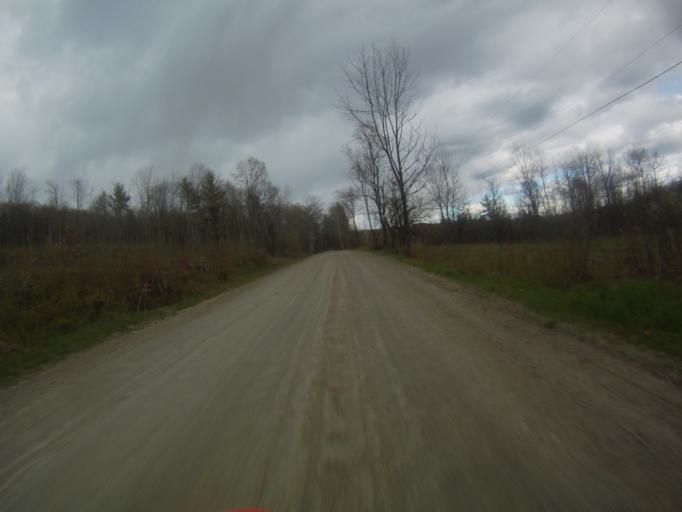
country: US
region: Vermont
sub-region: Addison County
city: Bristol
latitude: 44.0590
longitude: -73.0272
